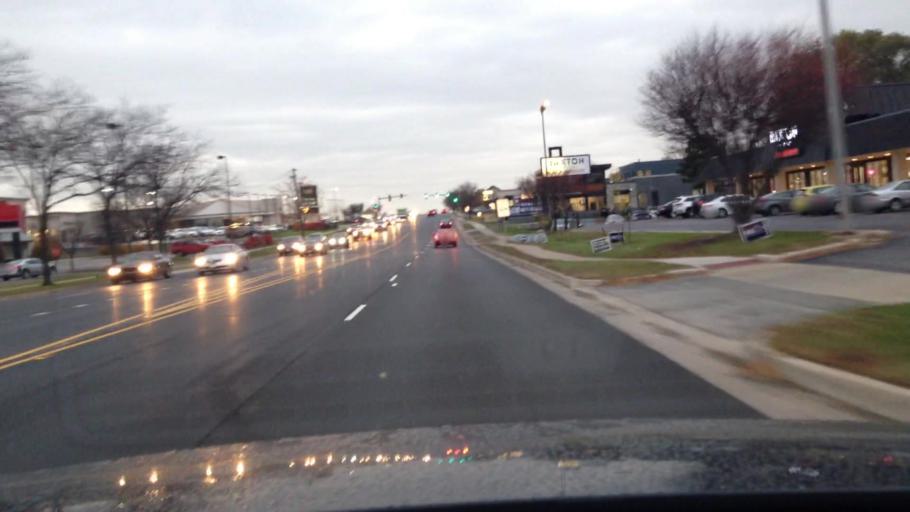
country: US
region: Illinois
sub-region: DuPage County
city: Lombard
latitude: 41.8600
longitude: -88.0205
